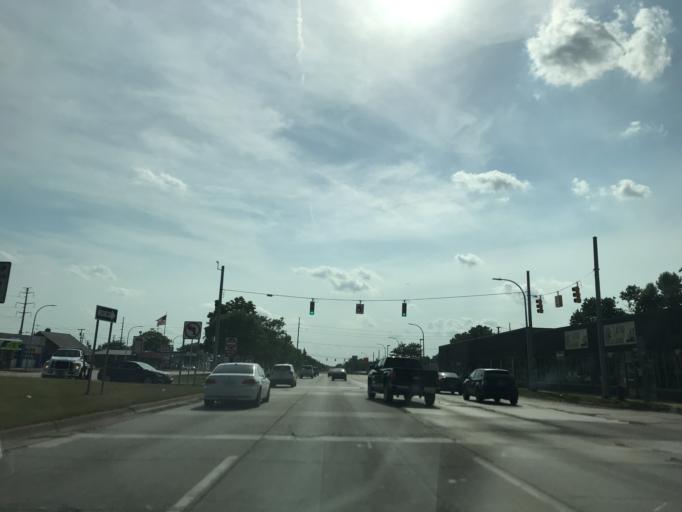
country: US
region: Michigan
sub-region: Wayne County
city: Wayne
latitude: 42.2839
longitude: -83.3603
